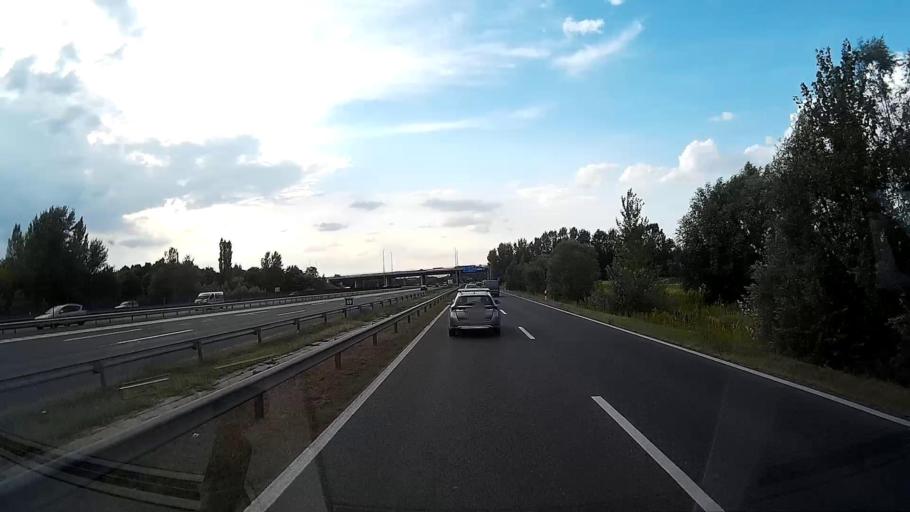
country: HU
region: Budapest
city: Budapest XV. keruelet
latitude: 47.5794
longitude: 19.1515
